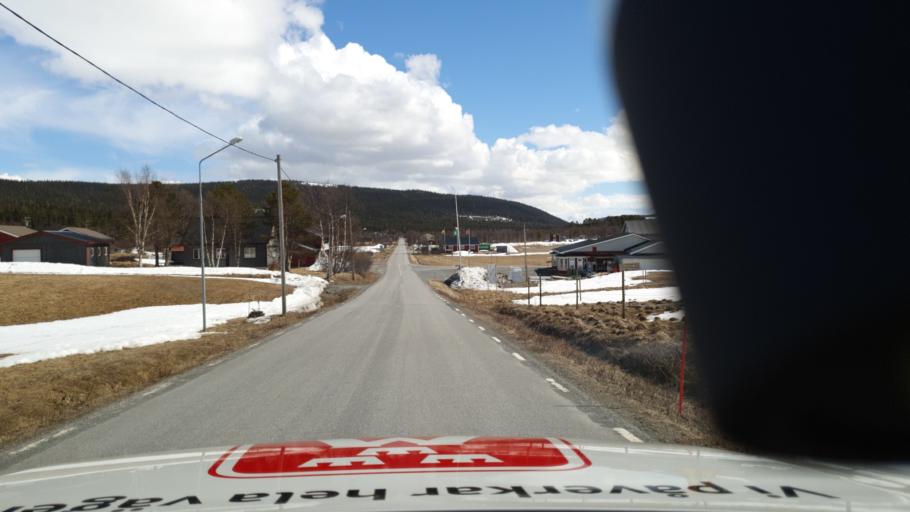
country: SE
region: Jaemtland
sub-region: Are Kommun
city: Are
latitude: 62.8533
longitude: 12.7884
